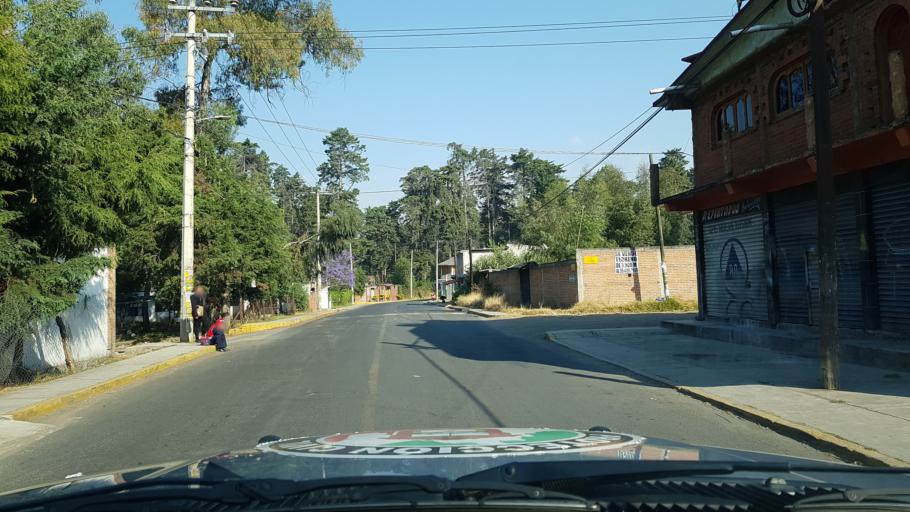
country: MX
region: Mexico
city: Ozumba de Alzate
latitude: 19.0594
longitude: -98.7785
